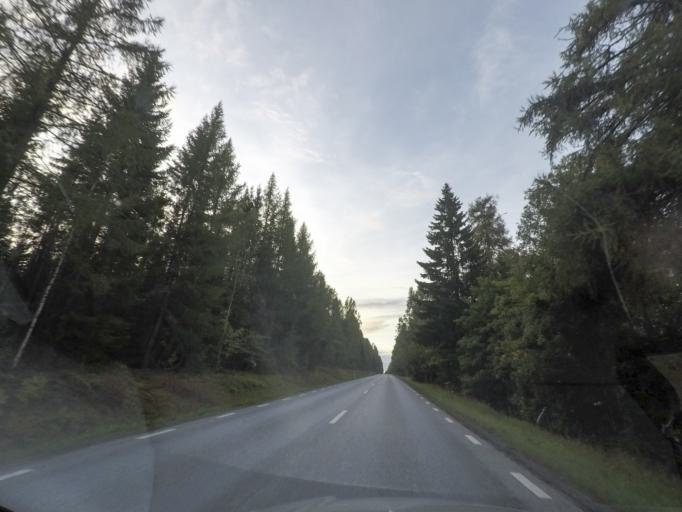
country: SE
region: OErebro
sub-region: Nora Kommun
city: As
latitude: 59.5744
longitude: 14.7163
